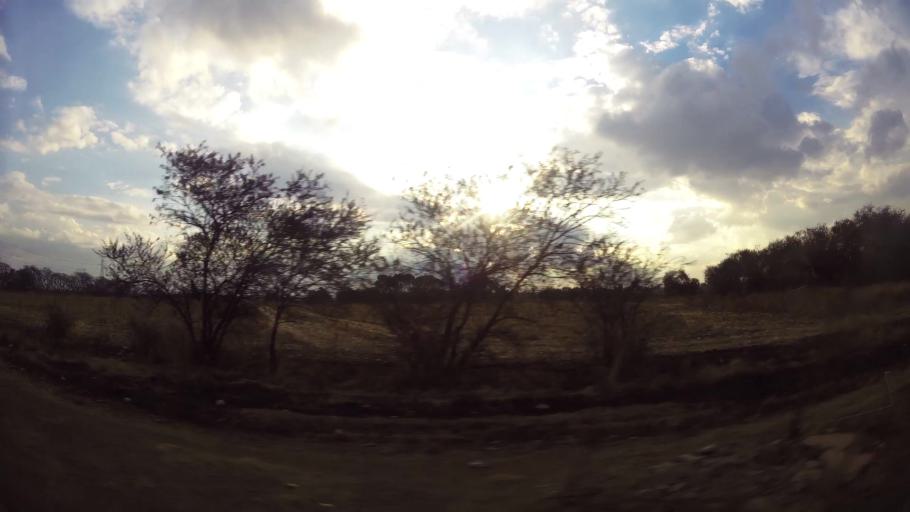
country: ZA
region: Gauteng
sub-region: Sedibeng District Municipality
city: Vanderbijlpark
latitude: -26.6629
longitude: 27.7980
